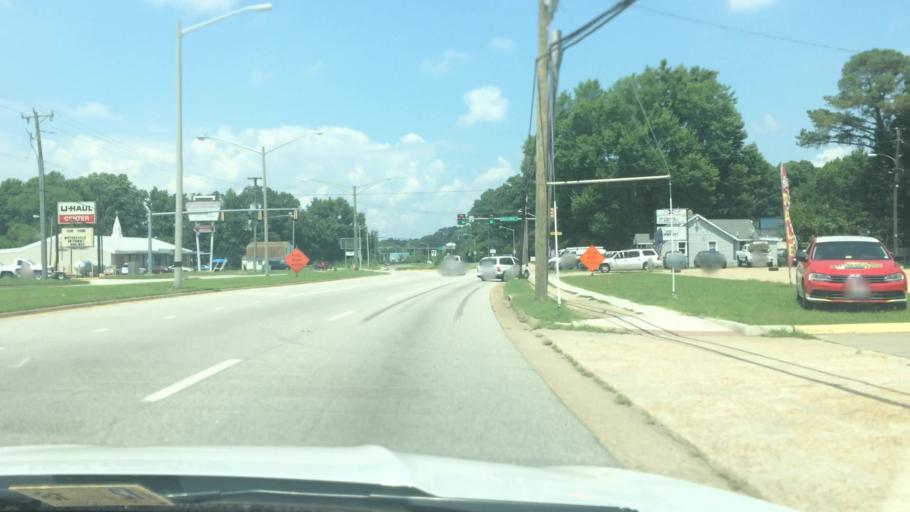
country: US
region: Virginia
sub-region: York County
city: Yorktown
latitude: 37.1385
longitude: -76.5461
